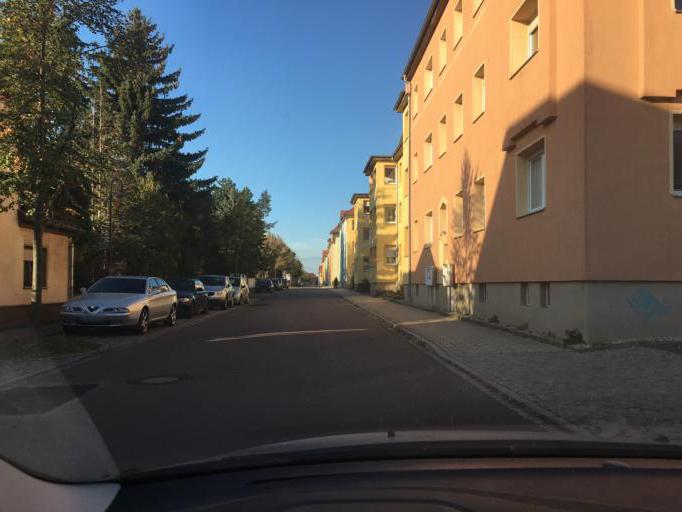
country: DE
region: Saxony-Anhalt
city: Lutzen
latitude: 51.2566
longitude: 12.1460
